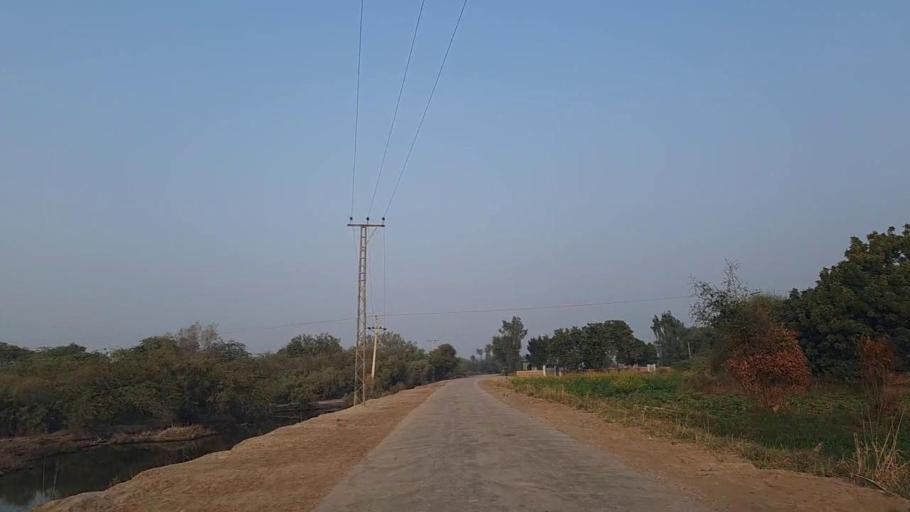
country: PK
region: Sindh
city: Nawabshah
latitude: 26.2471
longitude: 68.4633
